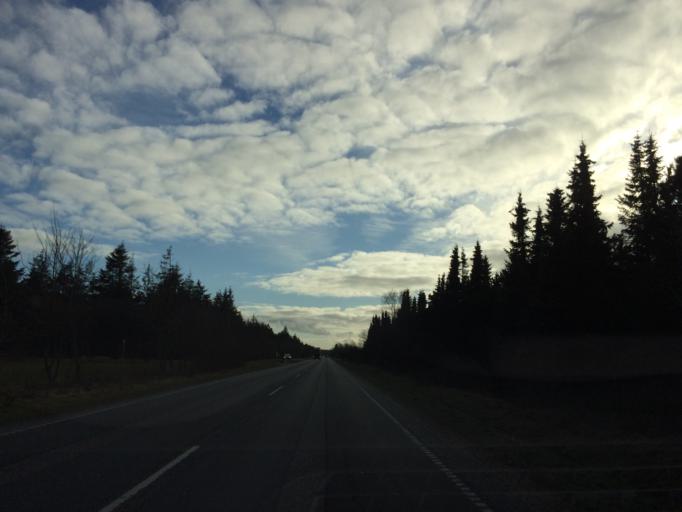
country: DK
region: Central Jutland
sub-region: Lemvig Kommune
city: Lemvig
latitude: 56.4922
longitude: 8.3002
